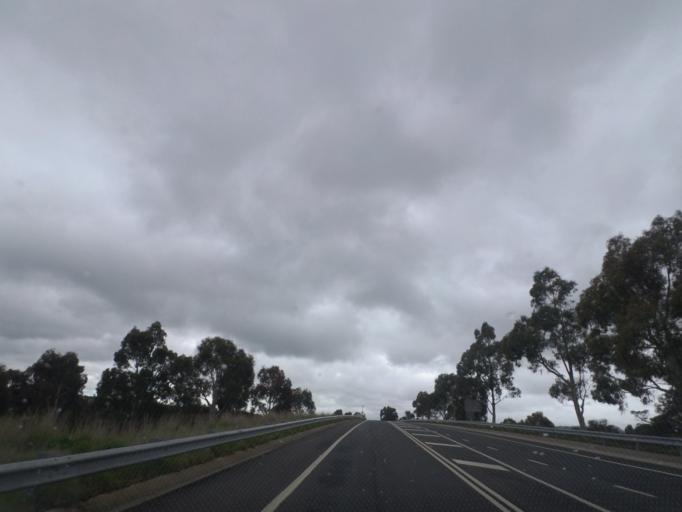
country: AU
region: Victoria
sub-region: Hume
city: Sunbury
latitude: -37.3216
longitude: 144.5251
